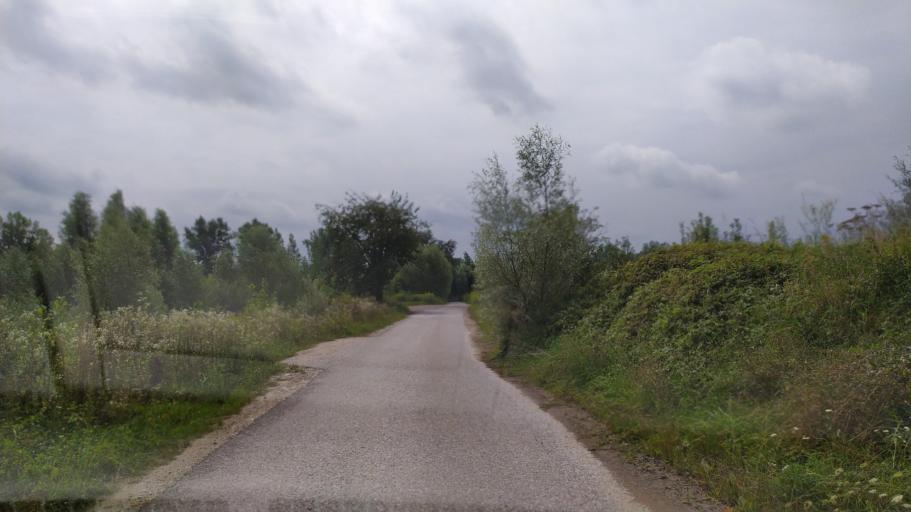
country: AT
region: Upper Austria
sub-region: Politischer Bezirk Perg
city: Bad Kreuzen
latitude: 48.1936
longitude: 14.7730
